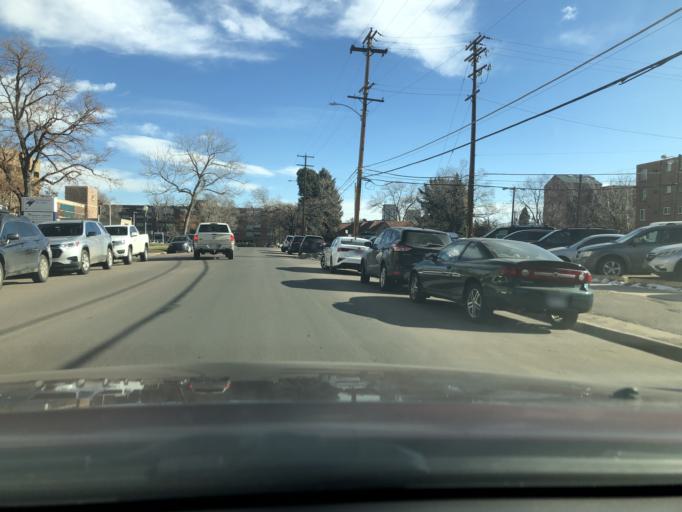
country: US
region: Colorado
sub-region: Denver County
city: Denver
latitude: 39.7460
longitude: -104.9670
